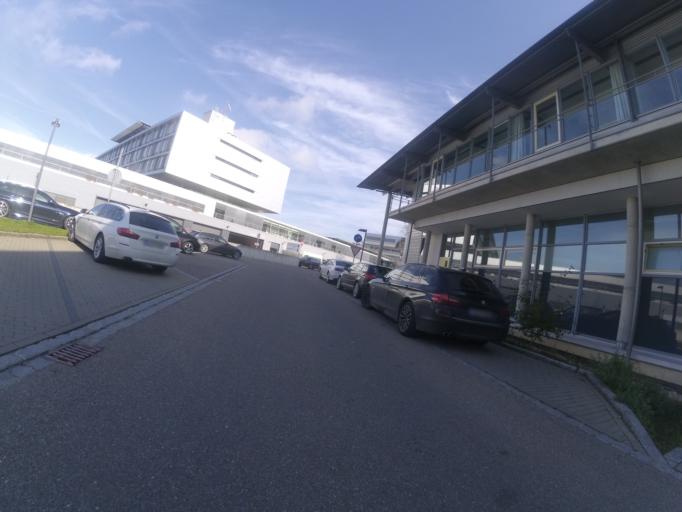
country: DE
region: Baden-Wuerttemberg
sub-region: Tuebingen Region
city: Dornstadt
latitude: 48.4216
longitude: 9.9515
